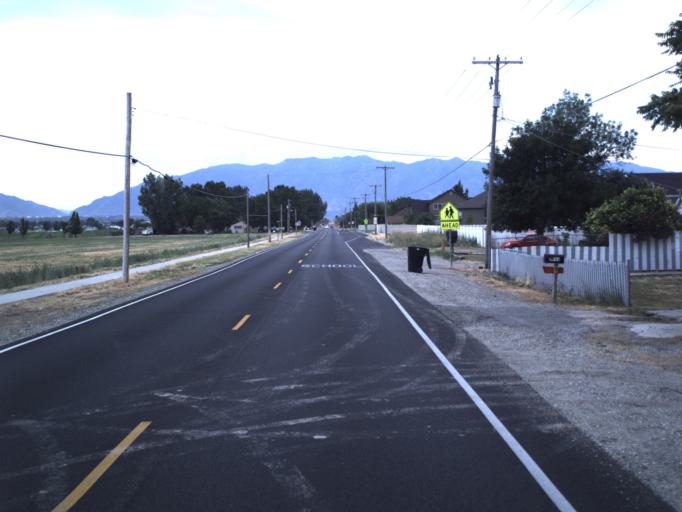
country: US
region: Utah
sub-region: Davis County
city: West Point
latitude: 41.0892
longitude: -112.0985
